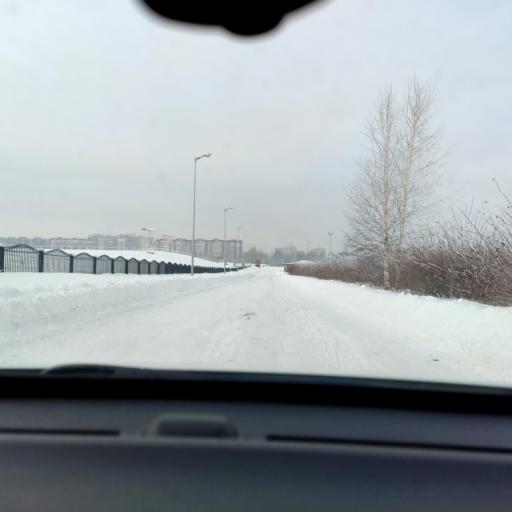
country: RU
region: Tatarstan
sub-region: Gorod Kazan'
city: Kazan
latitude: 55.7905
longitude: 49.2024
